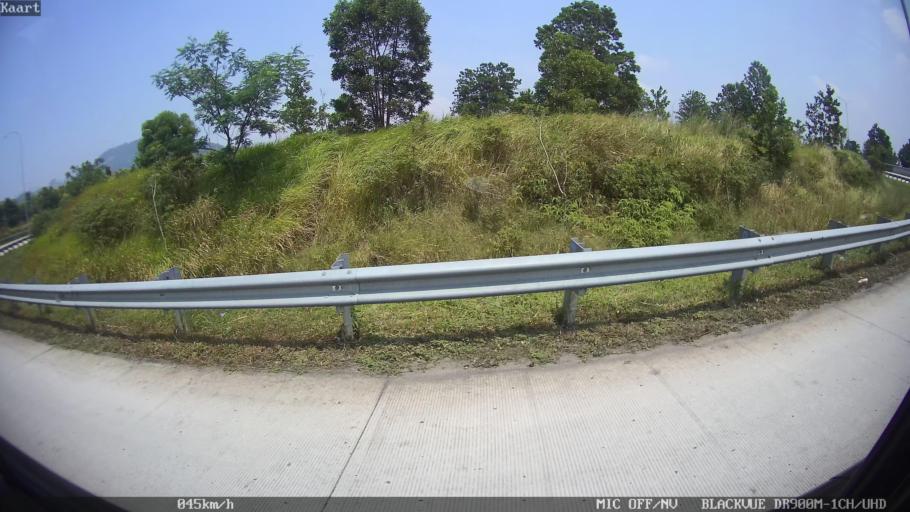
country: ID
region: Lampung
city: Panjang
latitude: -5.3965
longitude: 105.3511
